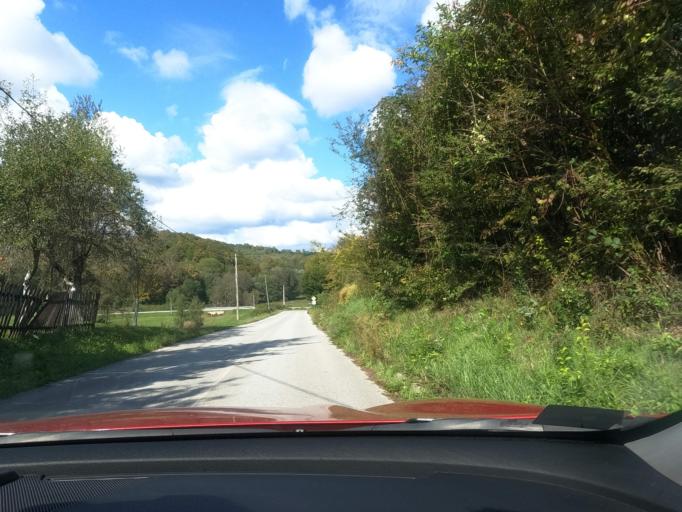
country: BA
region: Federation of Bosnia and Herzegovina
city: Velika Kladusa
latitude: 45.2115
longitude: 15.8176
